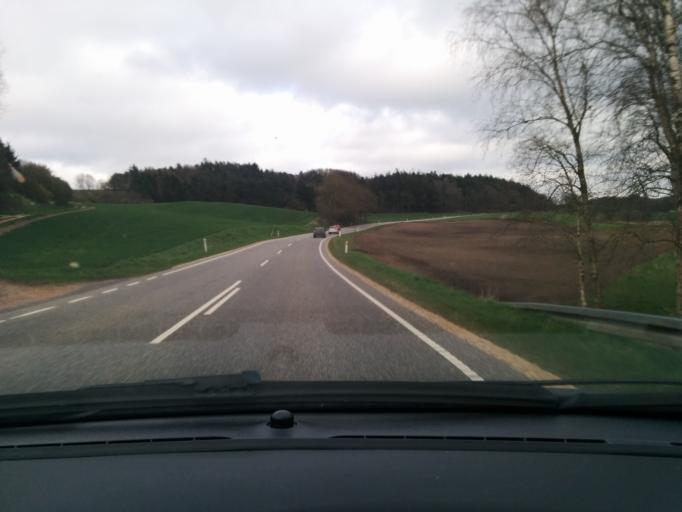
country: DK
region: Central Jutland
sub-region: Favrskov Kommune
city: Hammel
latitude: 56.2153
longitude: 9.7576
